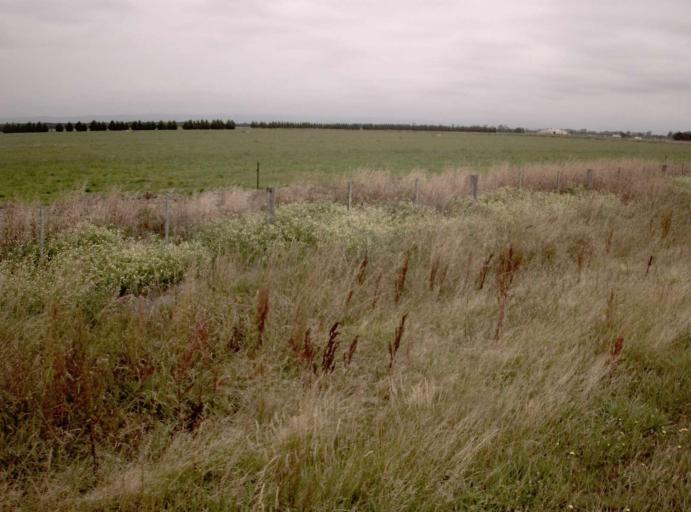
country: AU
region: Victoria
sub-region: Wellington
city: Heyfield
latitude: -38.0875
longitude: 146.7720
